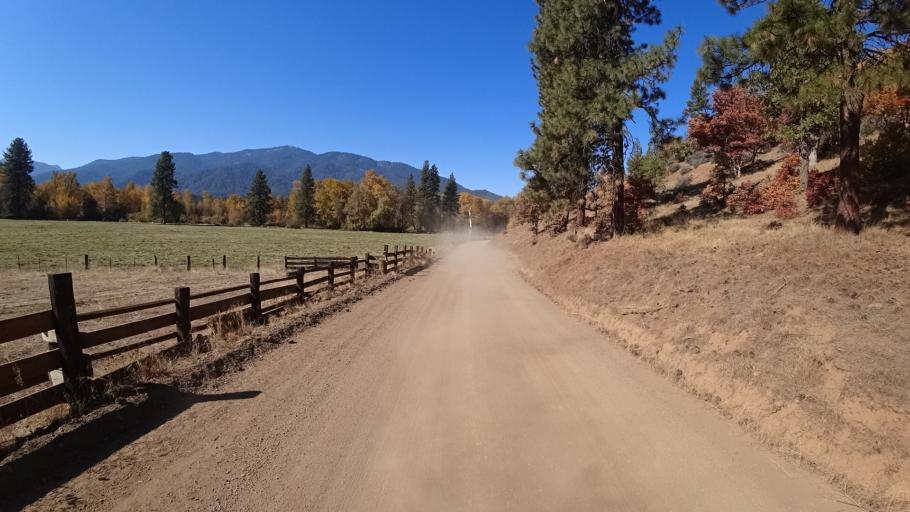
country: US
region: California
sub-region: Siskiyou County
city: Yreka
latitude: 41.6178
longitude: -122.9628
